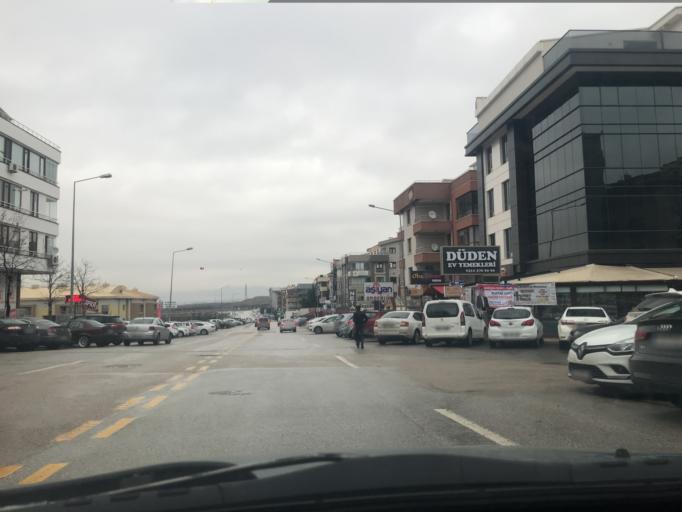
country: TR
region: Ankara
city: Batikent
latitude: 39.9121
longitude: 32.7677
